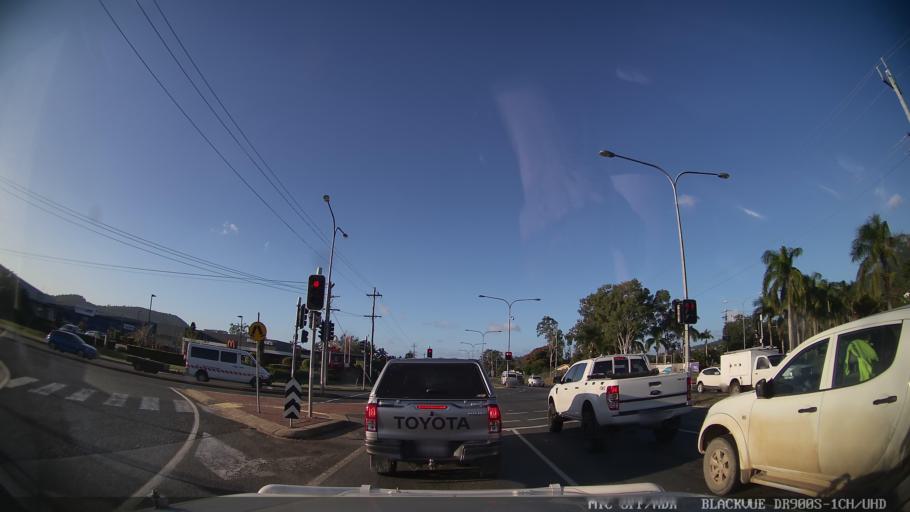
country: AU
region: Queensland
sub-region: Whitsunday
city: Proserpine
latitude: -20.2896
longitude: 148.6772
